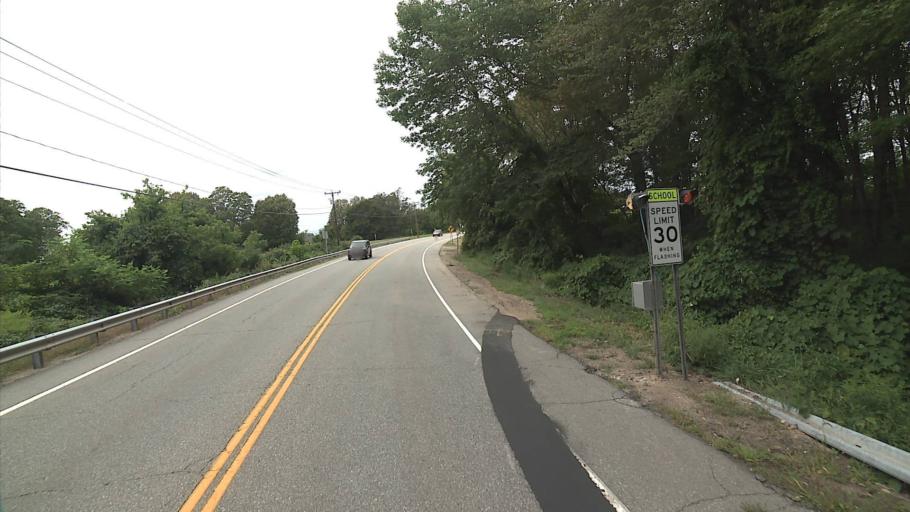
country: US
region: Connecticut
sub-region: Tolland County
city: Hebron
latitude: 41.6745
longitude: -72.4077
